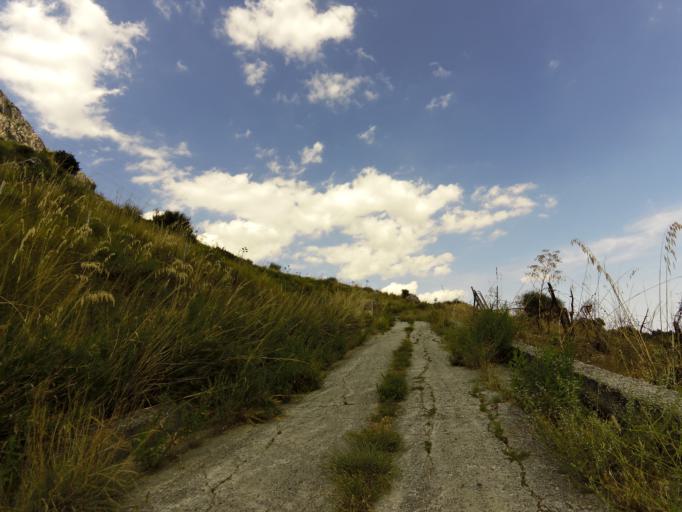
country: IT
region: Calabria
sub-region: Provincia di Reggio Calabria
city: Pazzano
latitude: 38.4717
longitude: 16.4592
